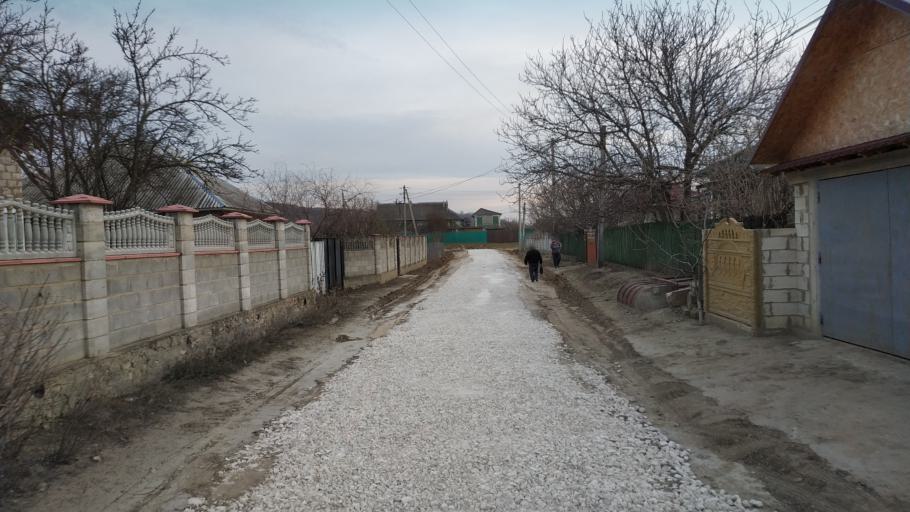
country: MD
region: Hincesti
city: Dancu
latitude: 46.7611
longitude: 28.2068
